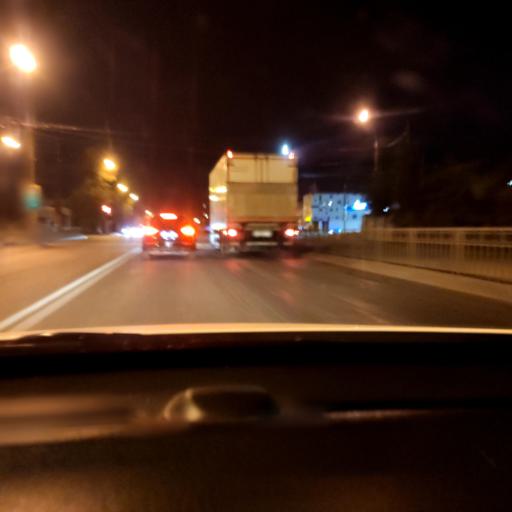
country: RU
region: Voronezj
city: Voronezh
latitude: 51.6432
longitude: 39.1540
